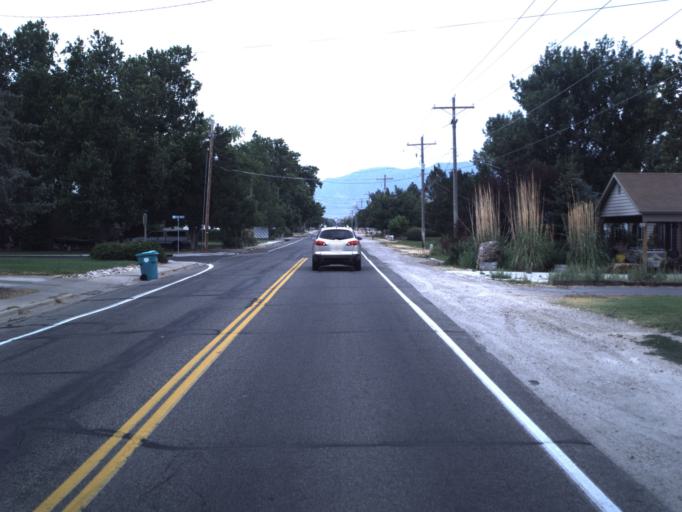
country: US
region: Utah
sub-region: Davis County
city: West Point
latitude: 41.1181
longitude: -112.0923
